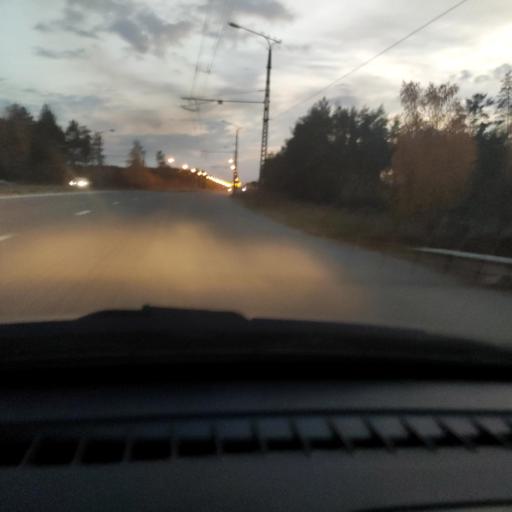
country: RU
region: Samara
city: Zhigulevsk
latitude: 53.5307
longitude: 49.5539
